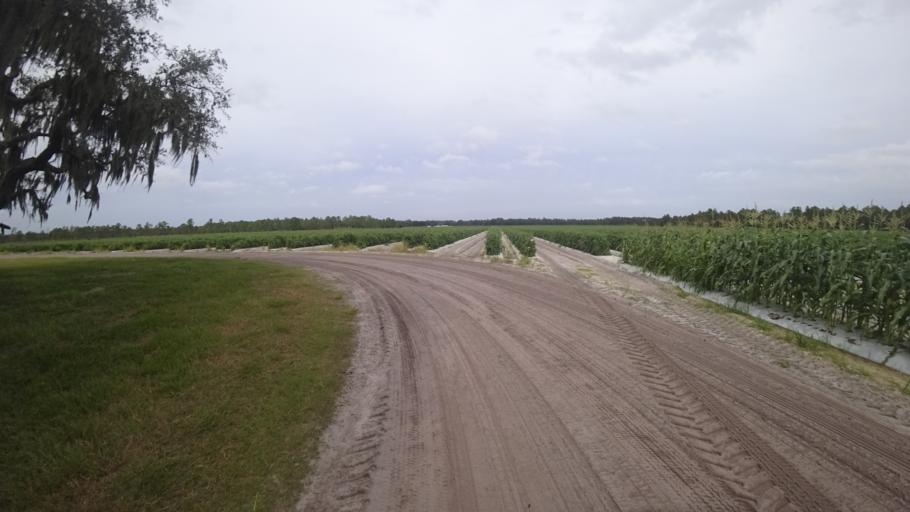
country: US
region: Florida
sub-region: Hillsborough County
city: Wimauma
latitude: 27.5625
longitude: -82.1360
